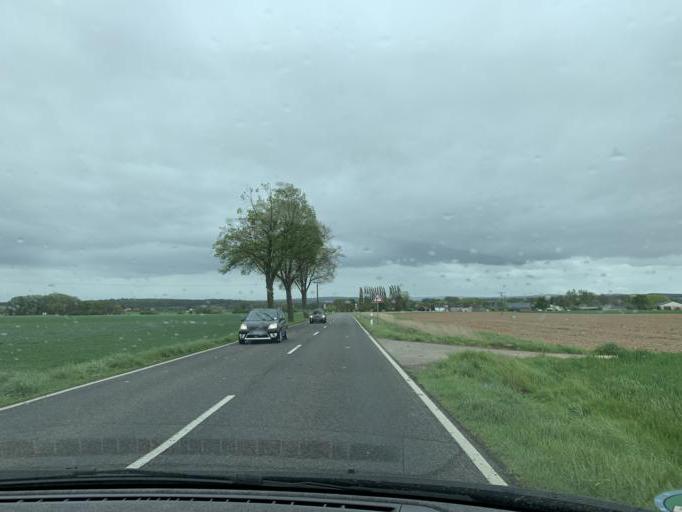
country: DE
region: North Rhine-Westphalia
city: Zulpich
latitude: 50.6758
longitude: 6.6451
